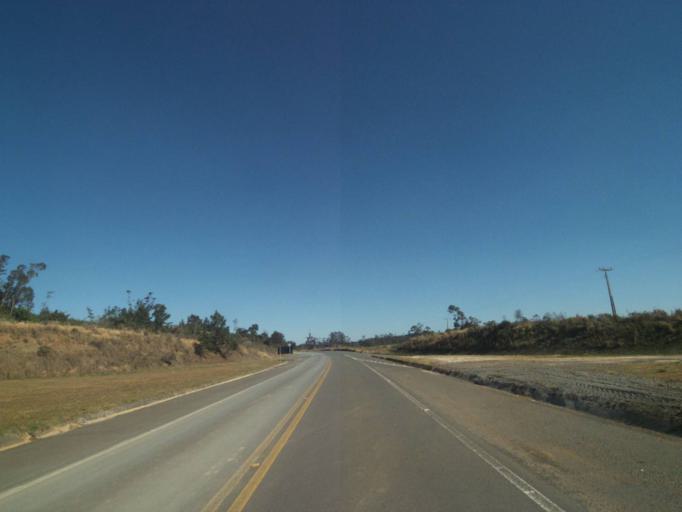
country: BR
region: Parana
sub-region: Tibagi
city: Tibagi
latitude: -24.8165
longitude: -50.4879
